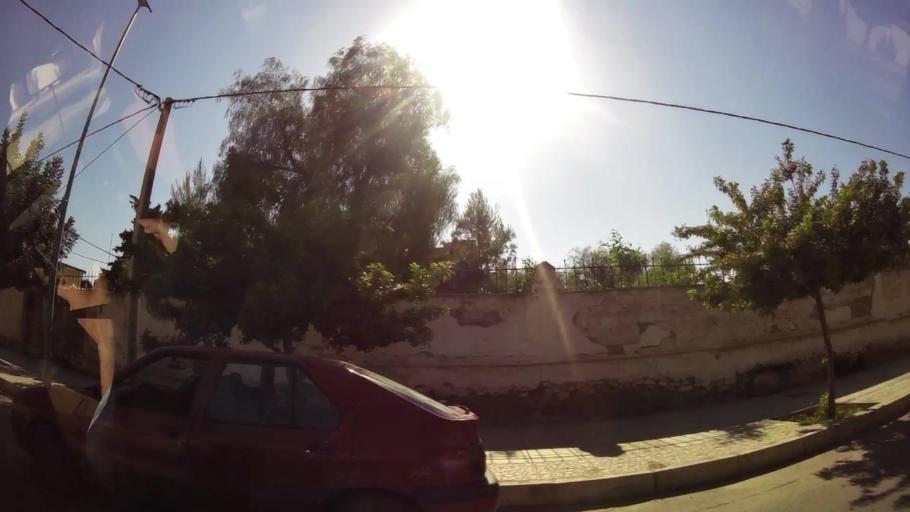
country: MA
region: Oriental
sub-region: Oujda-Angad
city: Oujda
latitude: 34.6902
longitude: -1.9213
